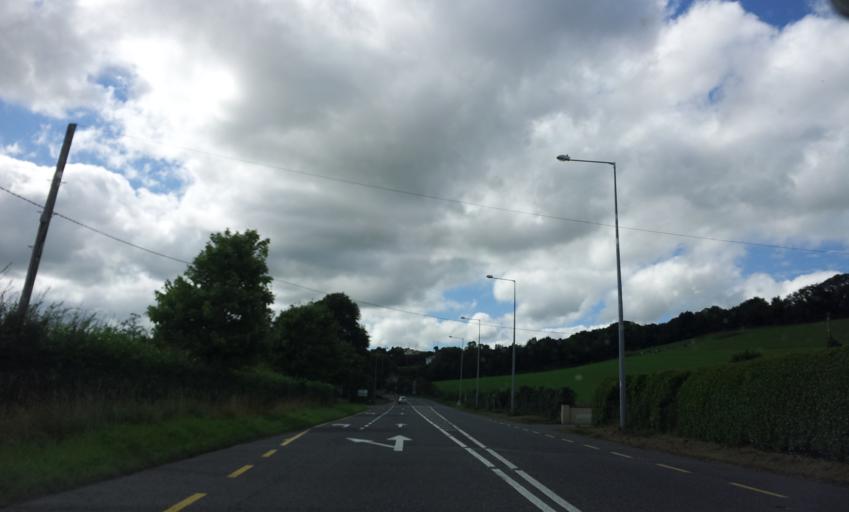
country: IE
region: Munster
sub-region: County Cork
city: Killumney
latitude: 51.8827
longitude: -8.6705
